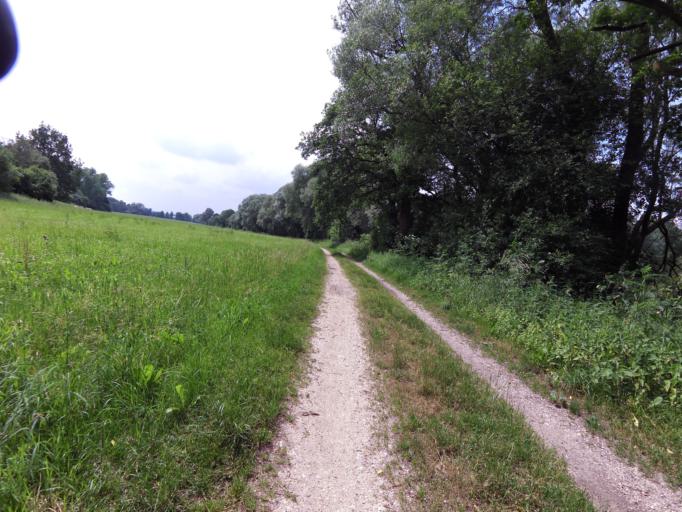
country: DE
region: Bavaria
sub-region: Upper Bavaria
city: Haag an der Amper
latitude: 48.4573
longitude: 11.8501
